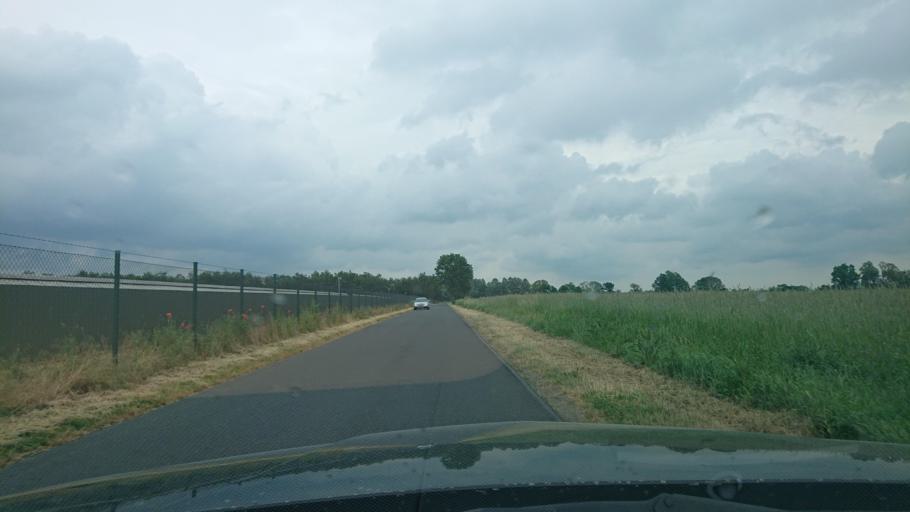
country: PL
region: Greater Poland Voivodeship
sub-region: Powiat gnieznienski
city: Czerniejewo
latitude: 52.4783
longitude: 17.5312
